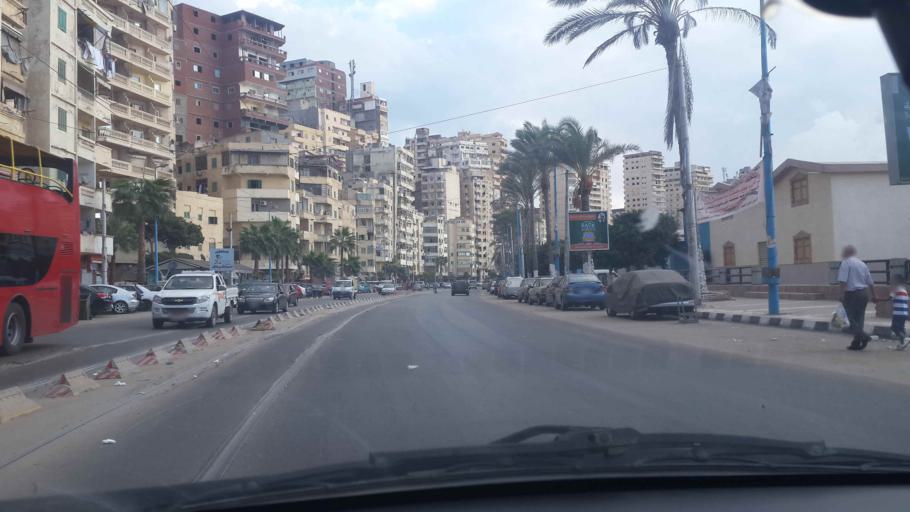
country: EG
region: Alexandria
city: Alexandria
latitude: 31.2085
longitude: 29.8793
